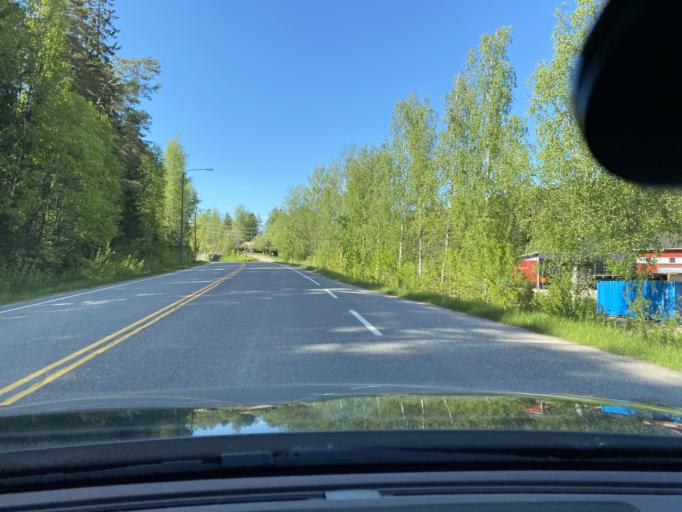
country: FI
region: Varsinais-Suomi
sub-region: Turku
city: Sauvo
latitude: 60.3476
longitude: 22.6821
